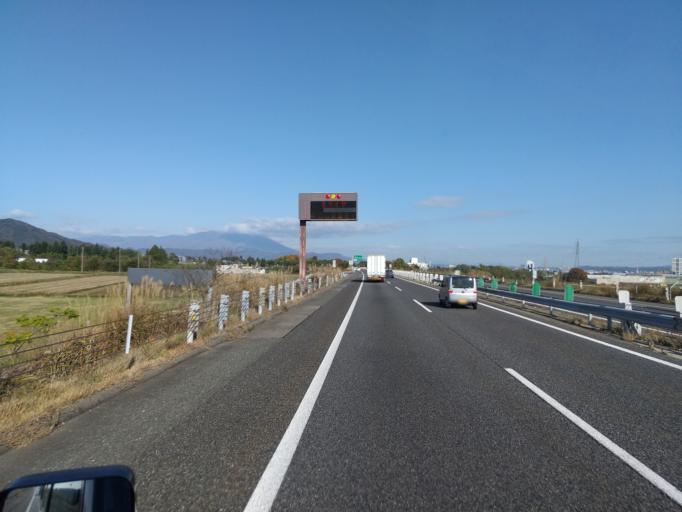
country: JP
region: Iwate
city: Morioka-shi
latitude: 39.6459
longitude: 141.1254
